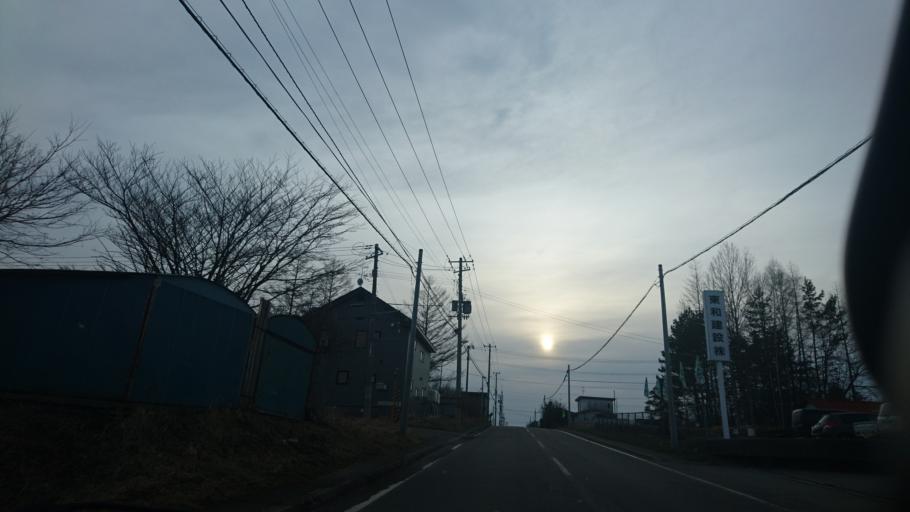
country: JP
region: Hokkaido
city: Otofuke
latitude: 42.9772
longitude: 143.2045
